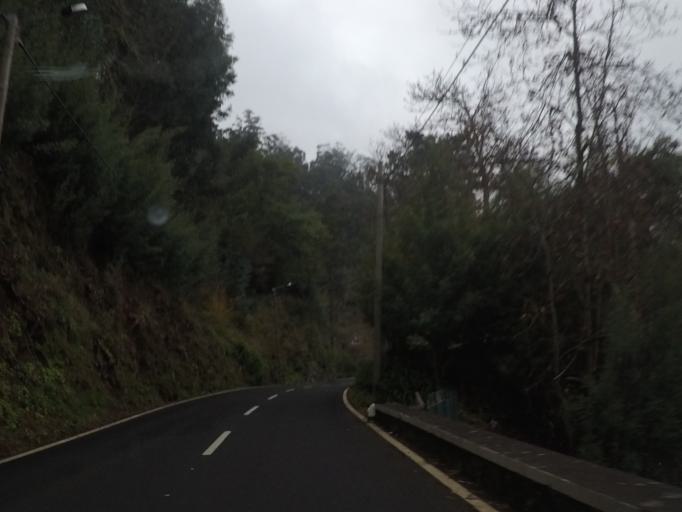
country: PT
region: Madeira
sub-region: Santa Cruz
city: Camacha
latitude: 32.6887
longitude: -16.8517
